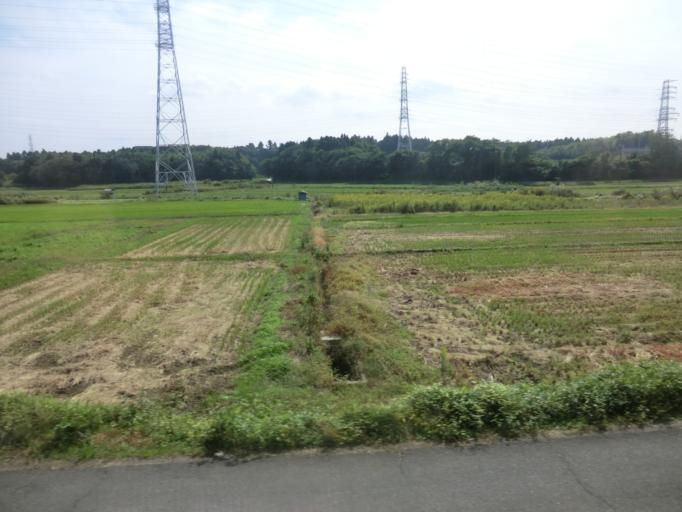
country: JP
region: Chiba
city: Shisui
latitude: 35.7152
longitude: 140.2666
